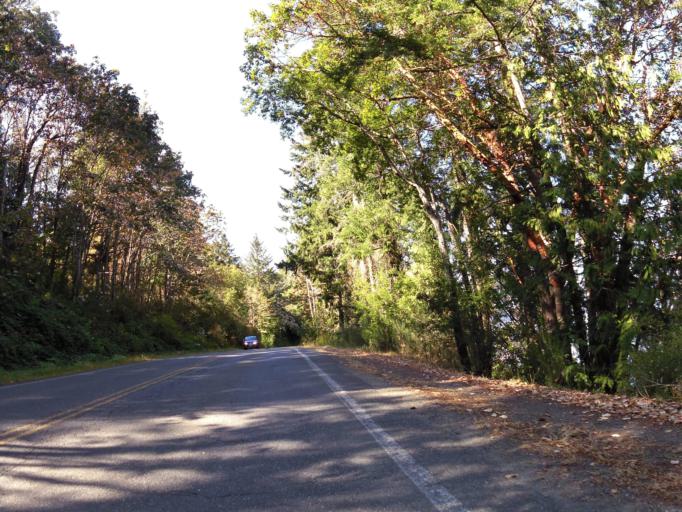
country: CA
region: British Columbia
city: North Saanich
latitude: 48.6251
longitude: -123.5271
